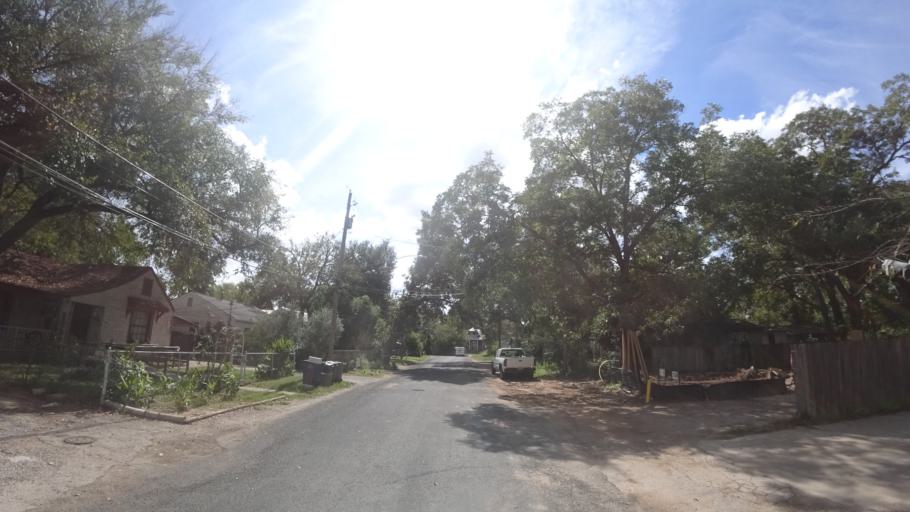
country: US
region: Texas
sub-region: Travis County
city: Austin
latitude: 30.2676
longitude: -97.7039
